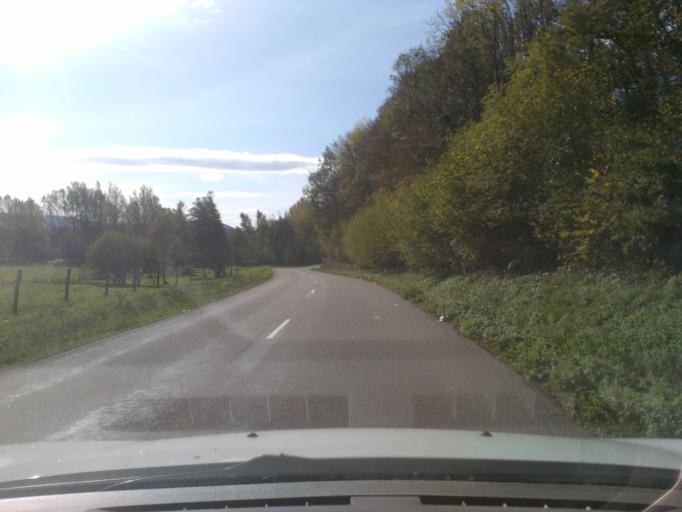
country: FR
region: Lorraine
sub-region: Departement des Vosges
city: Ban-de-Laveline
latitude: 48.2904
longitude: 7.0577
